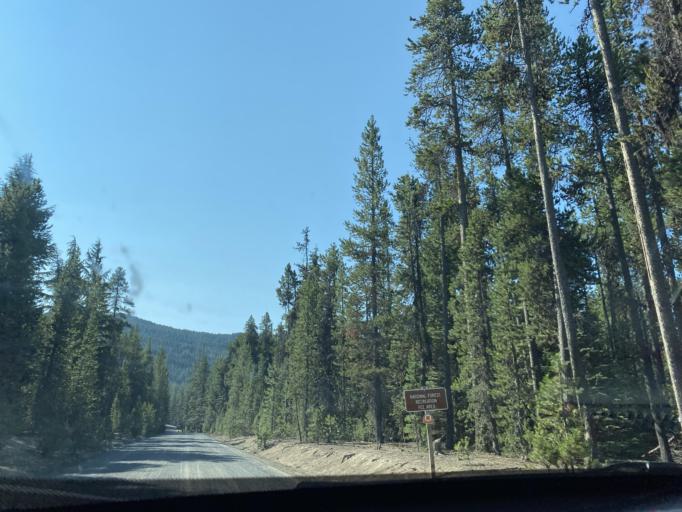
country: US
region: Oregon
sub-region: Deschutes County
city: Three Rivers
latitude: 43.7040
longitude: -121.2745
